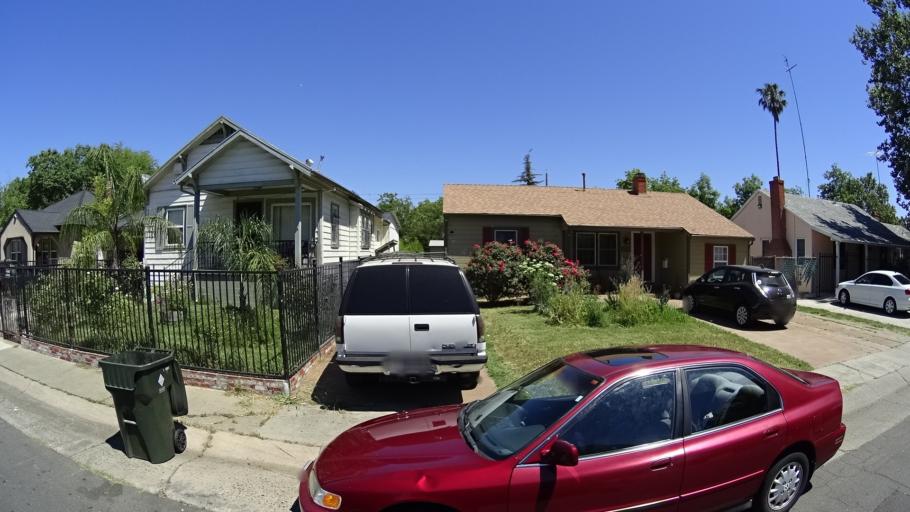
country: US
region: California
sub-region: Sacramento County
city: Parkway
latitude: 38.5412
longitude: -121.4598
